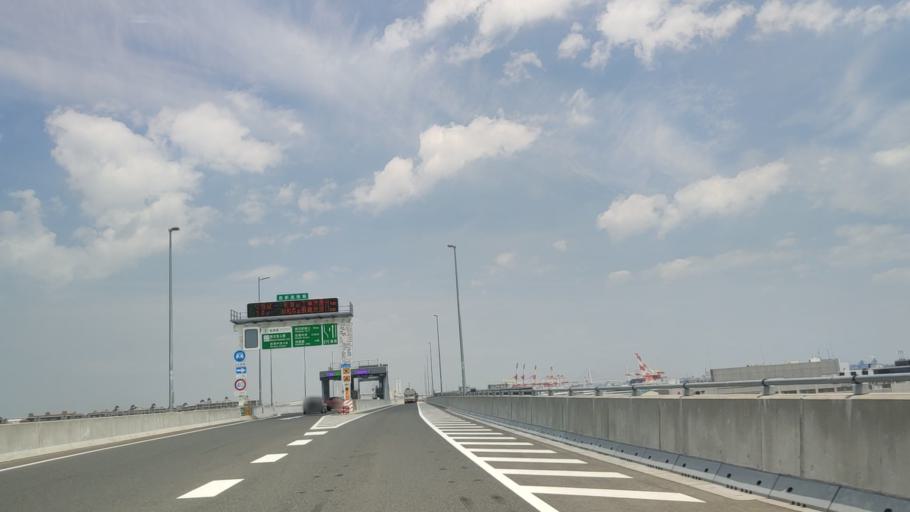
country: JP
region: Kanagawa
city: Yokohama
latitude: 35.4169
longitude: 139.6707
